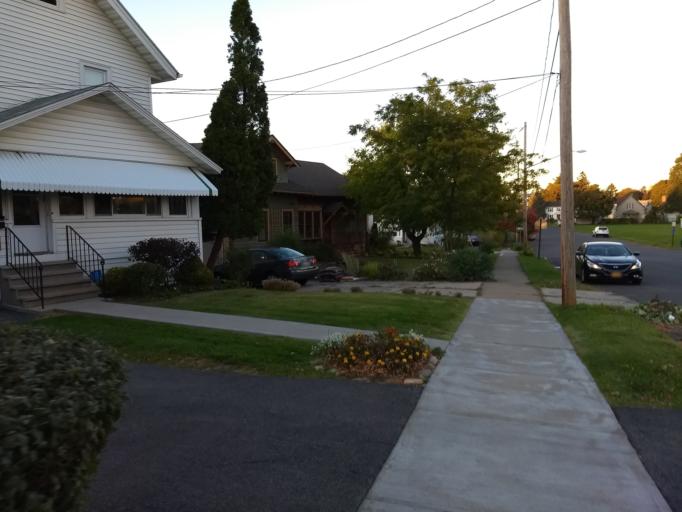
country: US
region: New York
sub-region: Onondaga County
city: Mattydale
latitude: 43.0748
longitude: -76.1494
